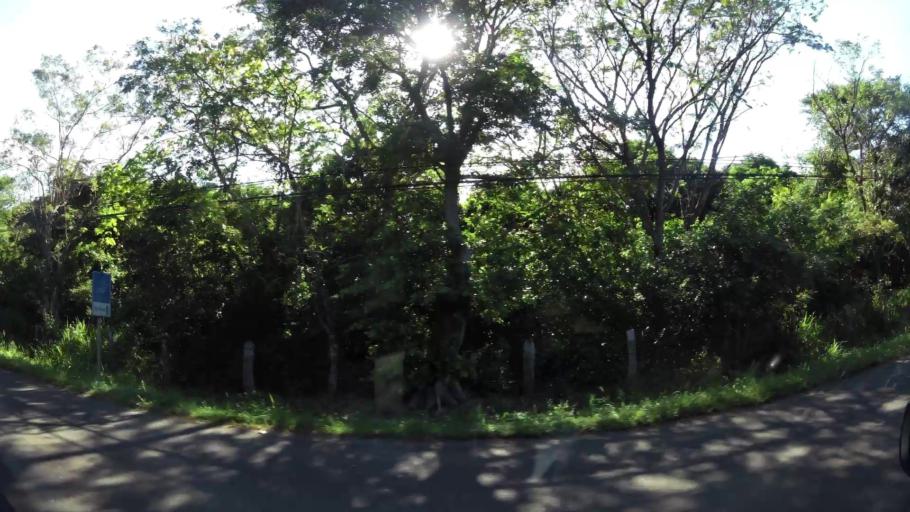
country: CR
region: Guanacaste
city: Sardinal
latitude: 10.5600
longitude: -85.5946
